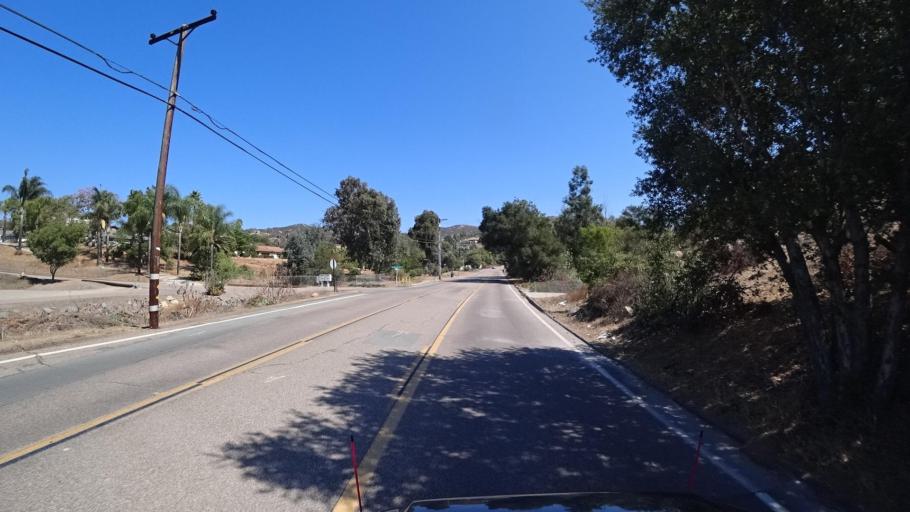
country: US
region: California
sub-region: San Diego County
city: Granite Hills
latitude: 32.8106
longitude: -116.9065
